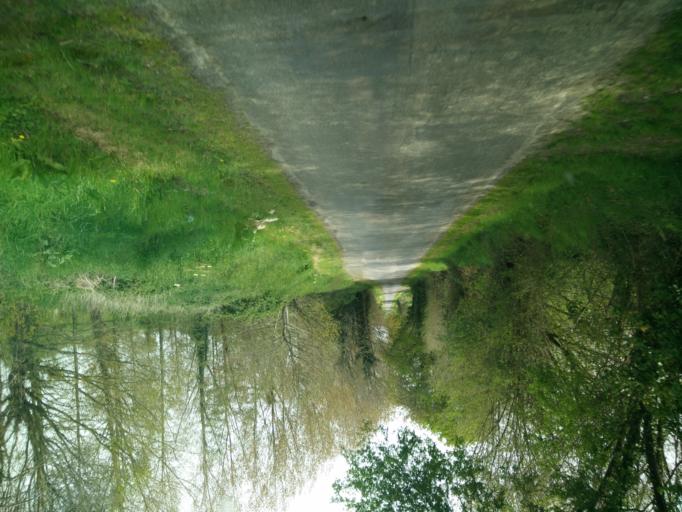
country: FR
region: Brittany
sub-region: Departement des Cotes-d'Armor
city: Matignon
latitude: 48.5850
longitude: -2.2467
